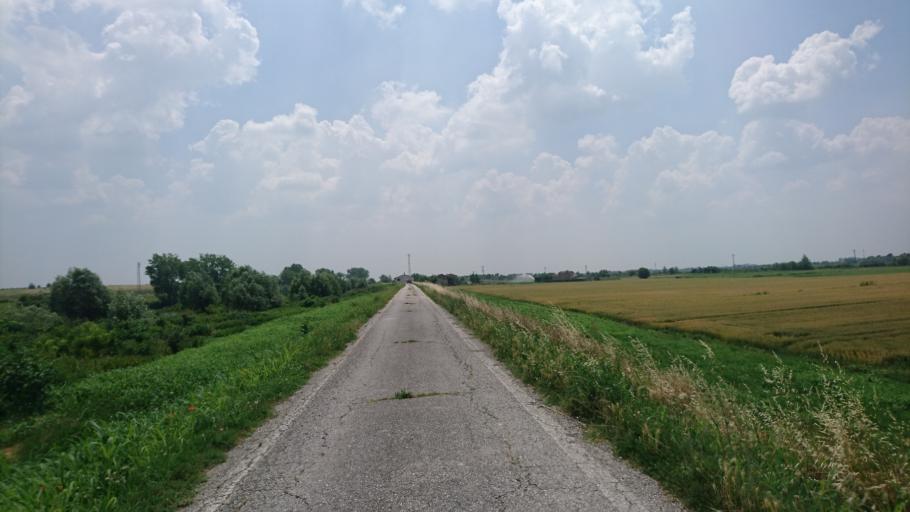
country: IT
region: Veneto
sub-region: Provincia di Venezia
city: Valli
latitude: 45.2230
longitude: 12.1585
